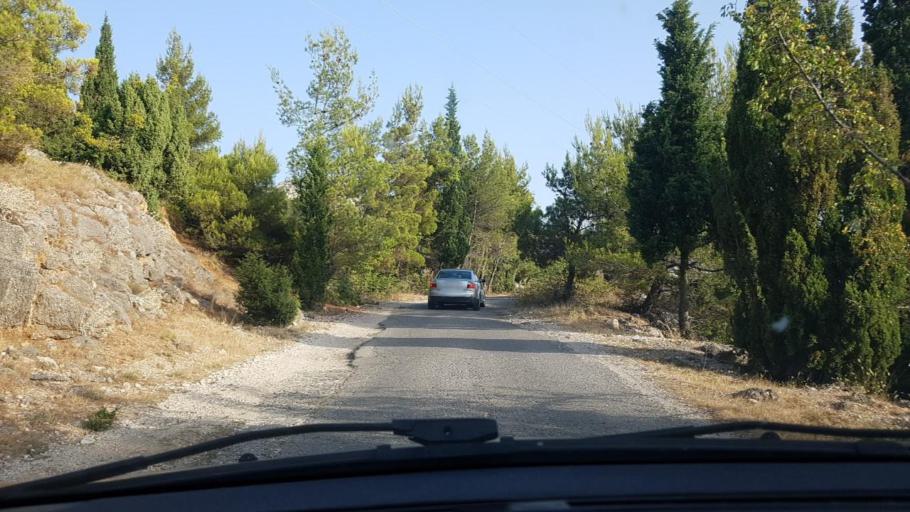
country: BA
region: Federation of Bosnia and Herzegovina
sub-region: Hercegovacko-Bosanski Kanton
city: Mostar
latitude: 43.3509
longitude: 17.8233
